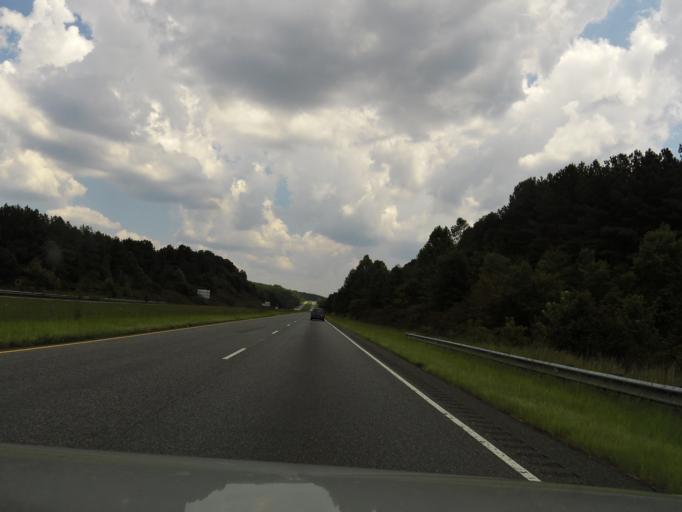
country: US
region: North Carolina
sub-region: Rutherford County
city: Rutherfordton
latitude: 35.2854
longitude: -82.0383
